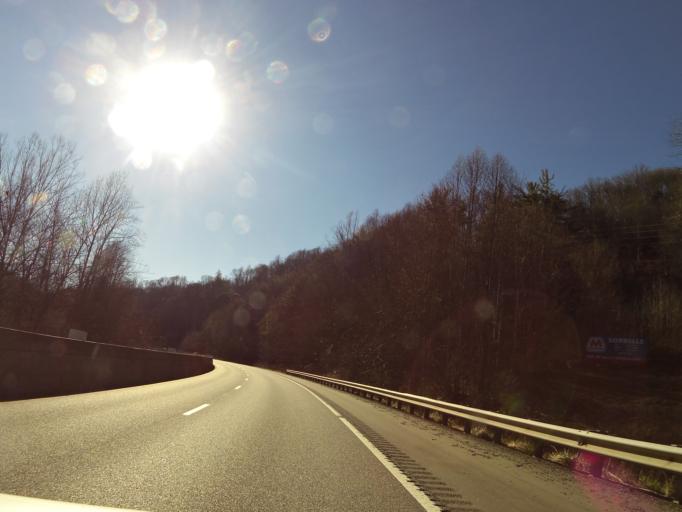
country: US
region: North Carolina
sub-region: Haywood County
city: Cove Creek
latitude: 35.6463
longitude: -82.9972
